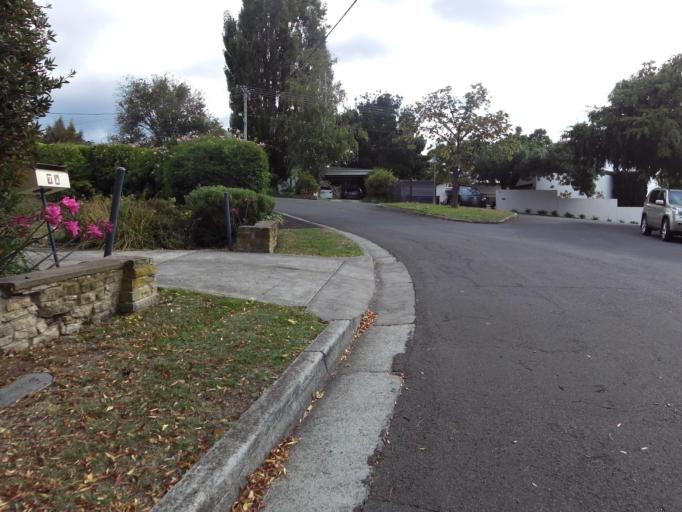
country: AU
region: Tasmania
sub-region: Kingborough
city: Taroona
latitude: -42.9331
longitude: 147.3592
